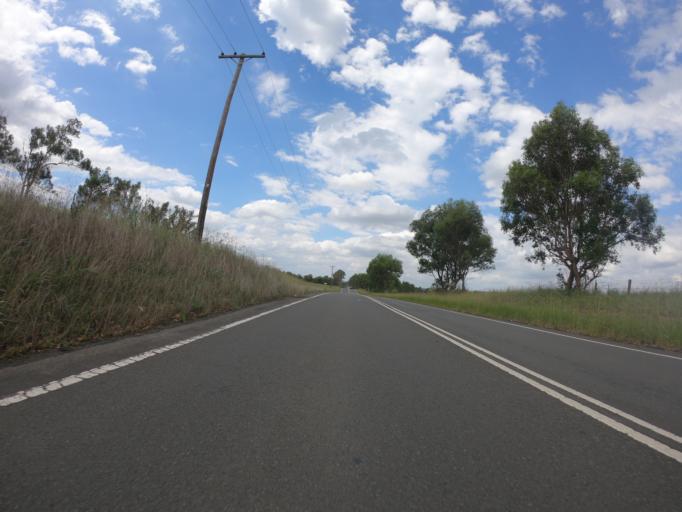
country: AU
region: New South Wales
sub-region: Liverpool
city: Luddenham
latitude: -33.8393
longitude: 150.7460
